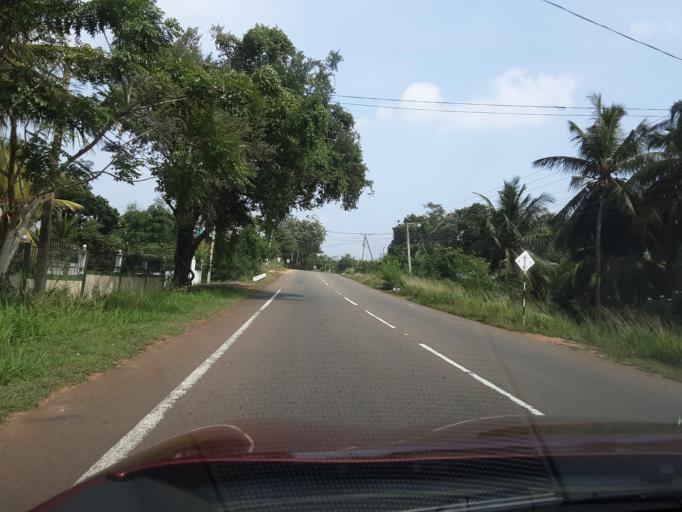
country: LK
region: North Central
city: Anuradhapura
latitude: 8.3379
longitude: 80.5022
